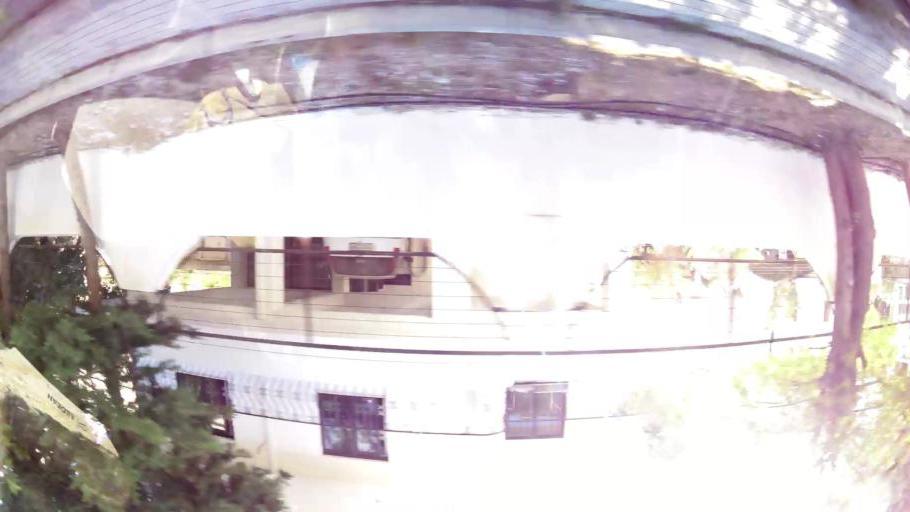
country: GR
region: Attica
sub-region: Nomarchia Anatolikis Attikis
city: Voula
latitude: 37.8406
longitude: 23.7759
